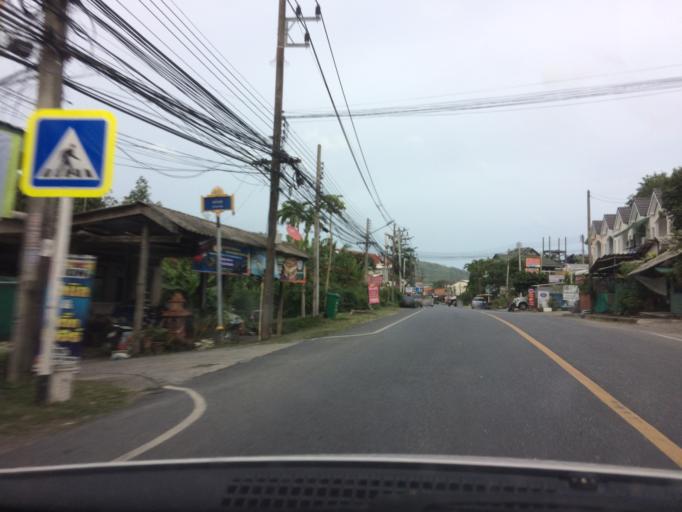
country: TH
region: Phuket
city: Ban Ratsada
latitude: 7.9057
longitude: 98.4072
